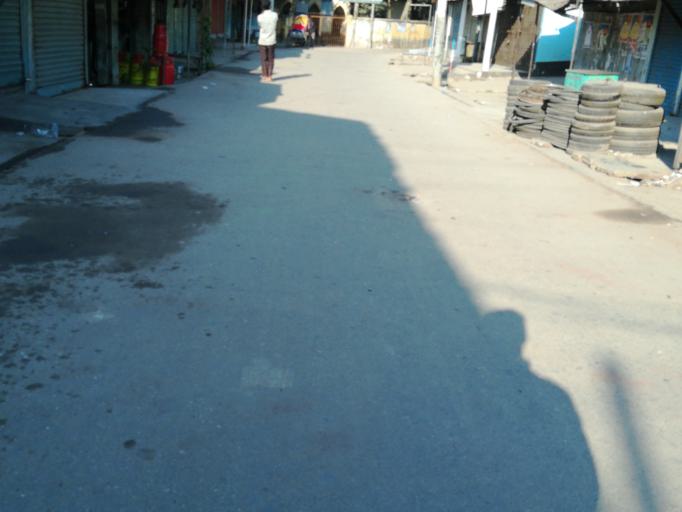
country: BD
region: Rangpur Division
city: Nageswari
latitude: 25.8145
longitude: 89.6488
